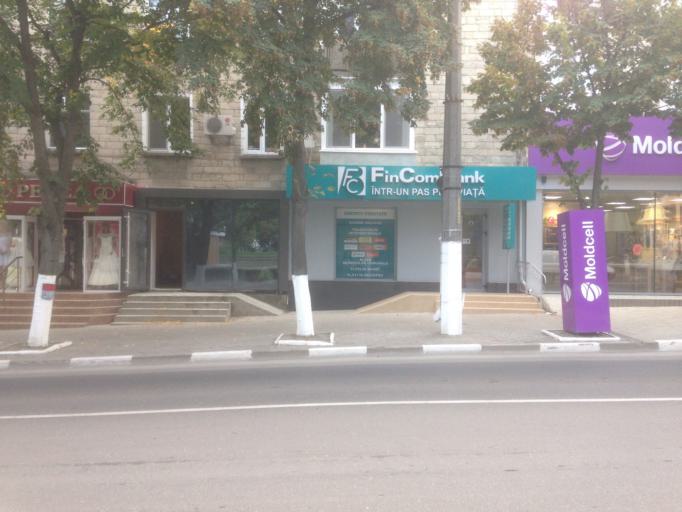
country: MD
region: Balti
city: Balti
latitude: 47.7631
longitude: 27.9290
